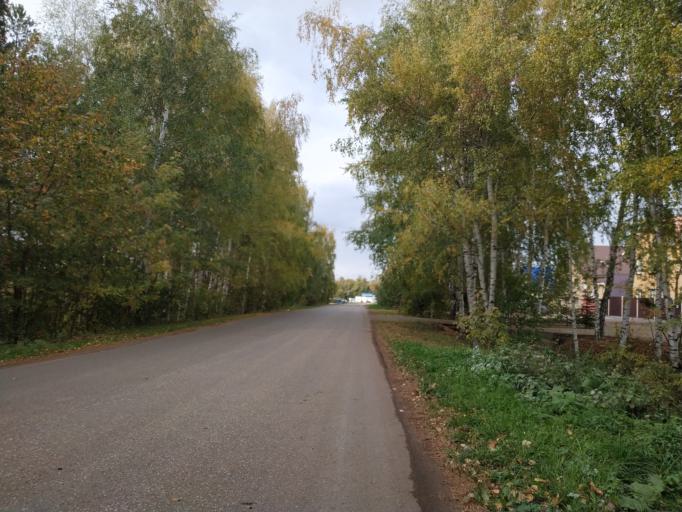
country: RU
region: Chuvashia
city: Ishley
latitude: 56.1303
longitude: 47.0886
